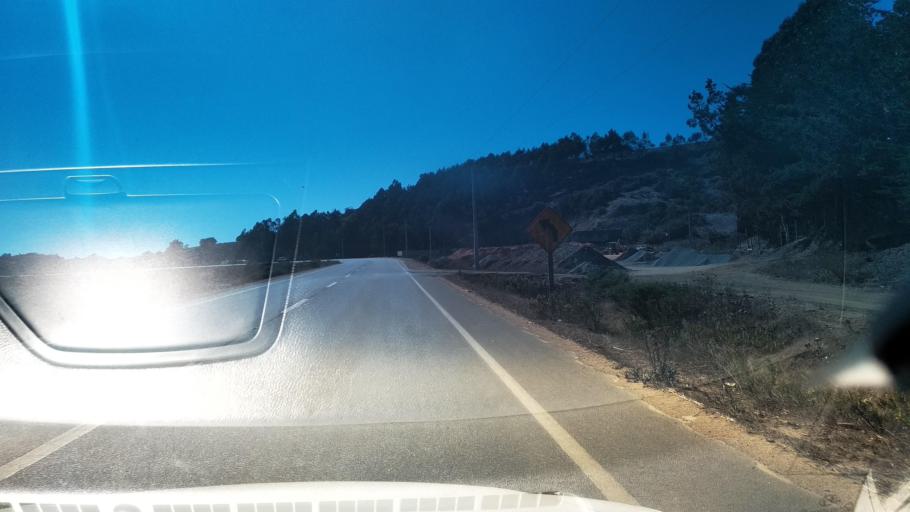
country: CL
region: O'Higgins
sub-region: Provincia de Colchagua
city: Santa Cruz
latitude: -34.4692
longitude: -72.0185
